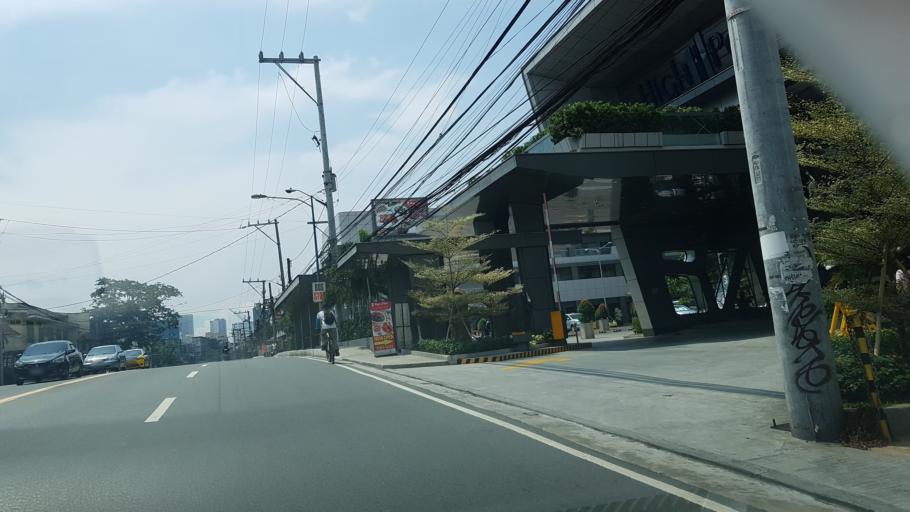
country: PH
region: Metro Manila
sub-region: San Juan
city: San Juan
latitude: 14.5908
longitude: 121.0333
